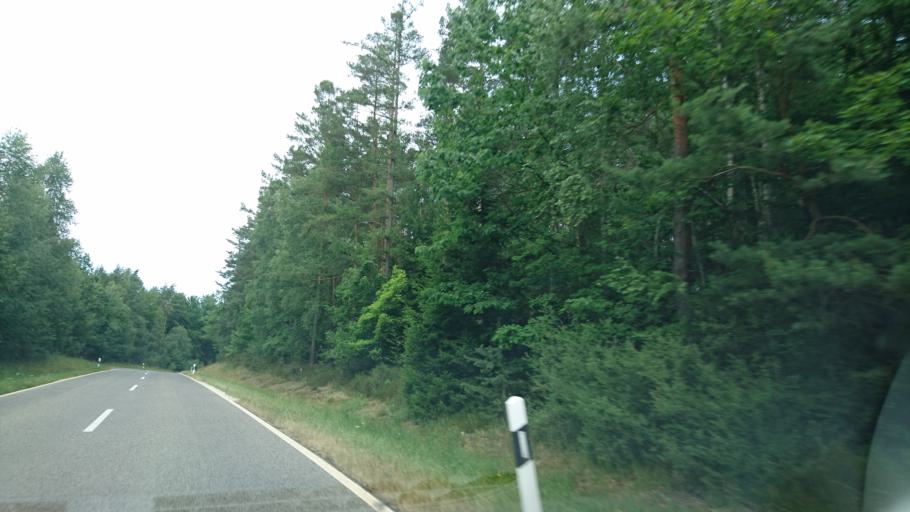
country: DE
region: Bavaria
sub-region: Regierungsbezirk Mittelfranken
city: Heideck
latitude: 49.1736
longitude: 11.1173
